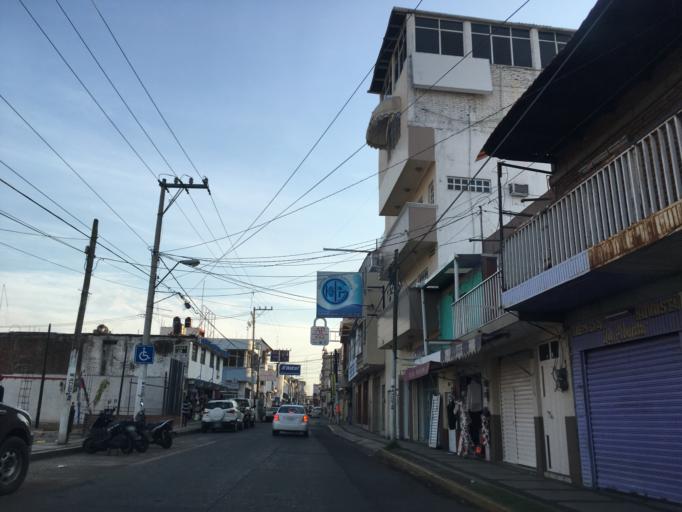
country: MX
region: Michoacan
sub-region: Los Reyes
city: La Higuerita (Colonia San Rafael)
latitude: 19.5928
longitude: -102.4732
